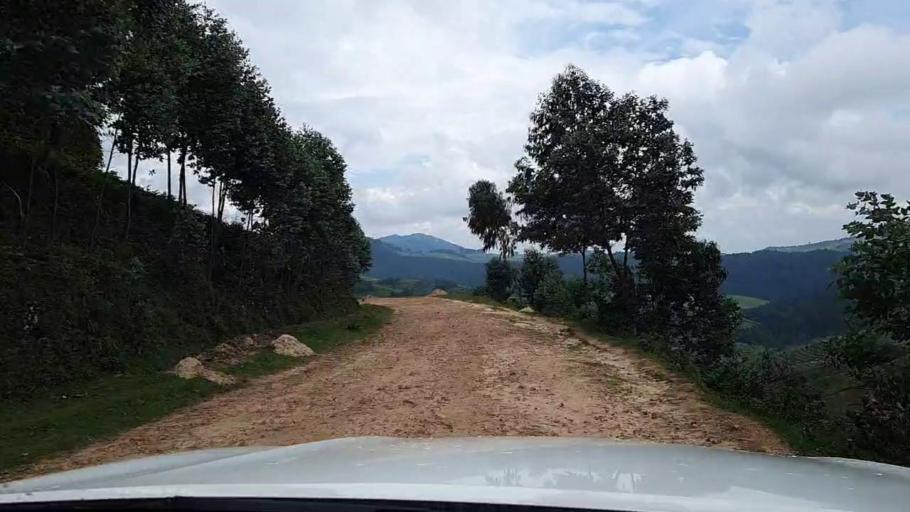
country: RW
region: Western Province
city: Kibuye
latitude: -2.2876
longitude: 29.3755
